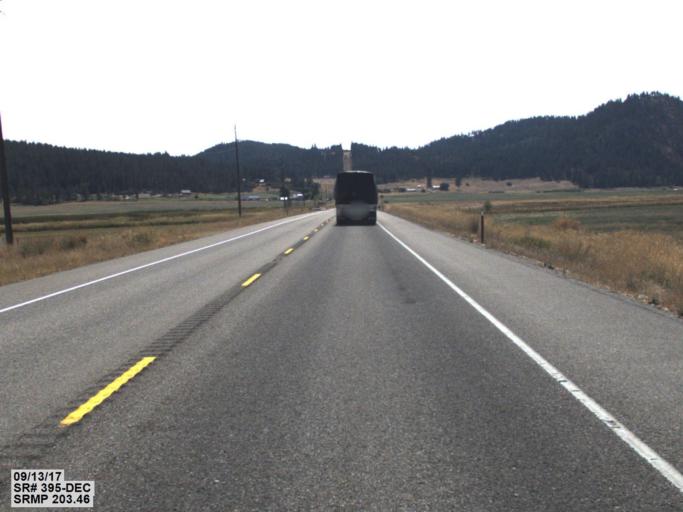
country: US
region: Washington
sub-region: Stevens County
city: Chewelah
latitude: 48.2233
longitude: -117.7154
